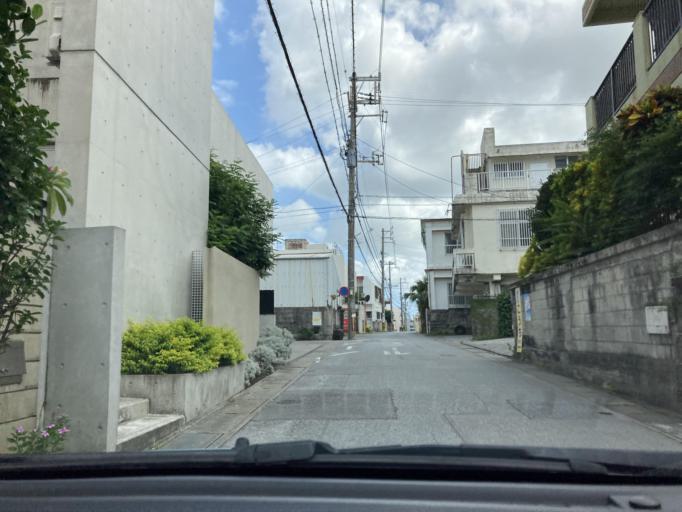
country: JP
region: Okinawa
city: Naha-shi
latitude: 26.1994
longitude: 127.6735
